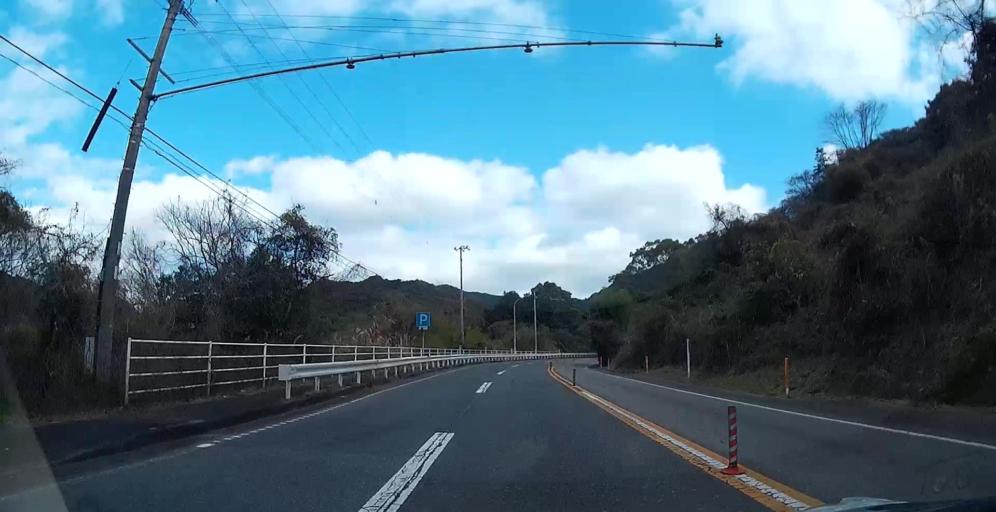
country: JP
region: Kumamoto
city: Yatsushiro
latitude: 32.3677
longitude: 130.5191
